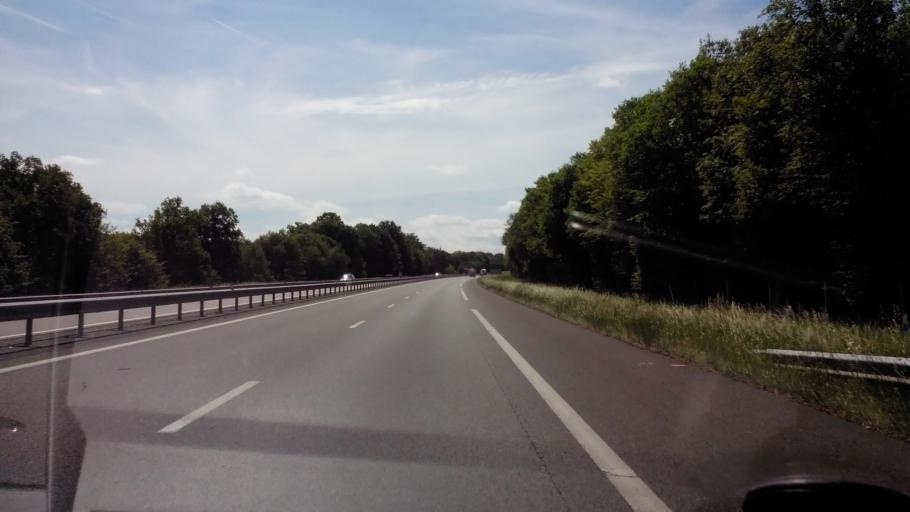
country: FR
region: Lorraine
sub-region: Departement de Meurthe-et-Moselle
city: Colombey-les-Belles
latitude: 48.5313
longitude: 5.9113
